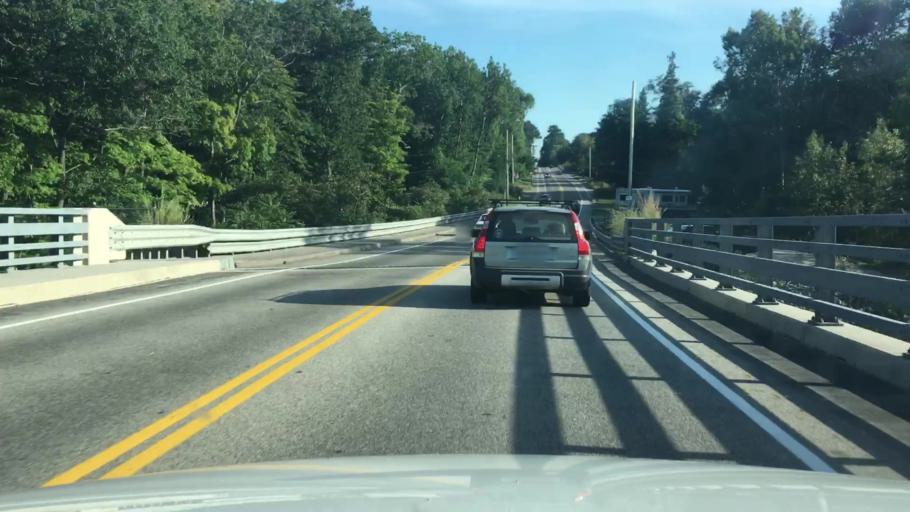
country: US
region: Maine
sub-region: Cumberland County
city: Falmouth
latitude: 43.7286
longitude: -70.2951
